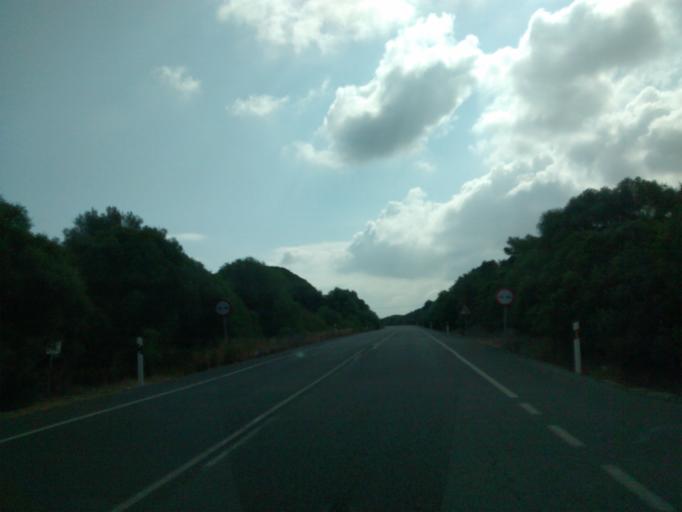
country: ES
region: Andalusia
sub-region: Provincia de Cadiz
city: Vejer de la Frontera
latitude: 36.2489
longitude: -5.9203
